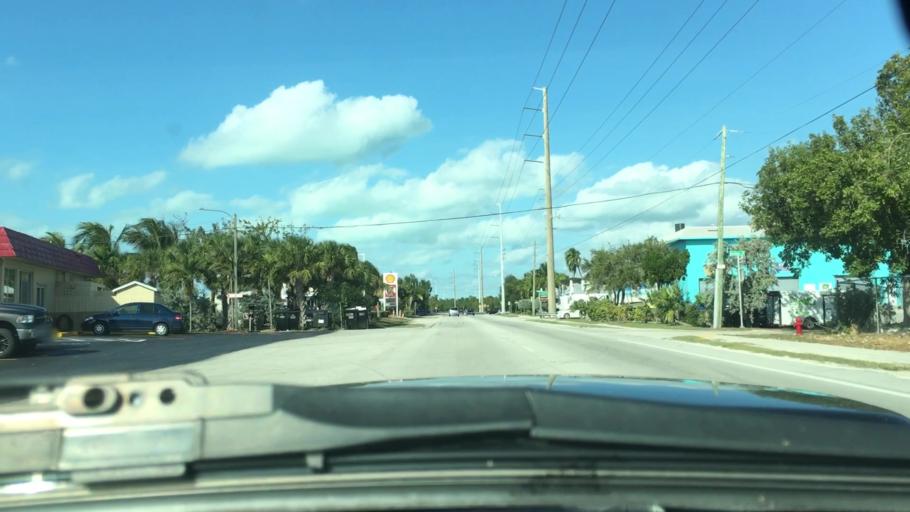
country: US
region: Florida
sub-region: Monroe County
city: Tavernier
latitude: 25.0166
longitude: -80.5114
